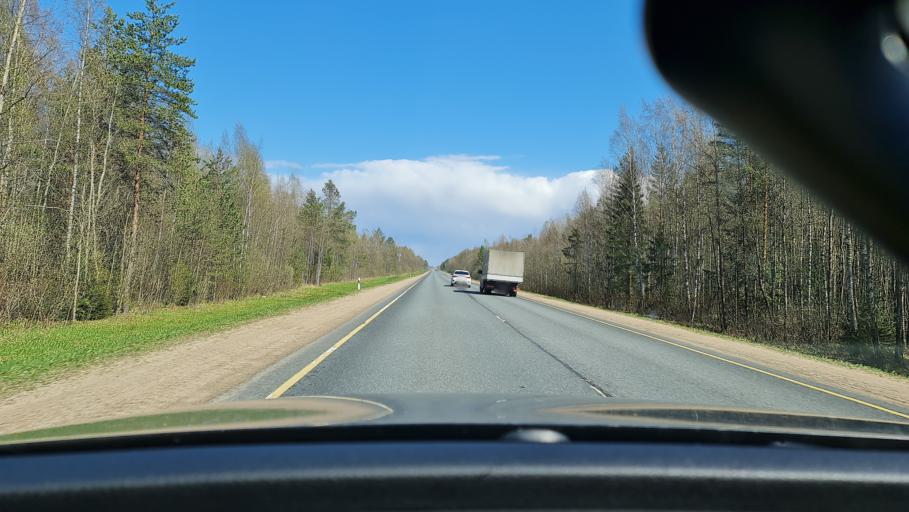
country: RU
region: Tverskaya
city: Rzhev
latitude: 56.2127
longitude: 34.1412
